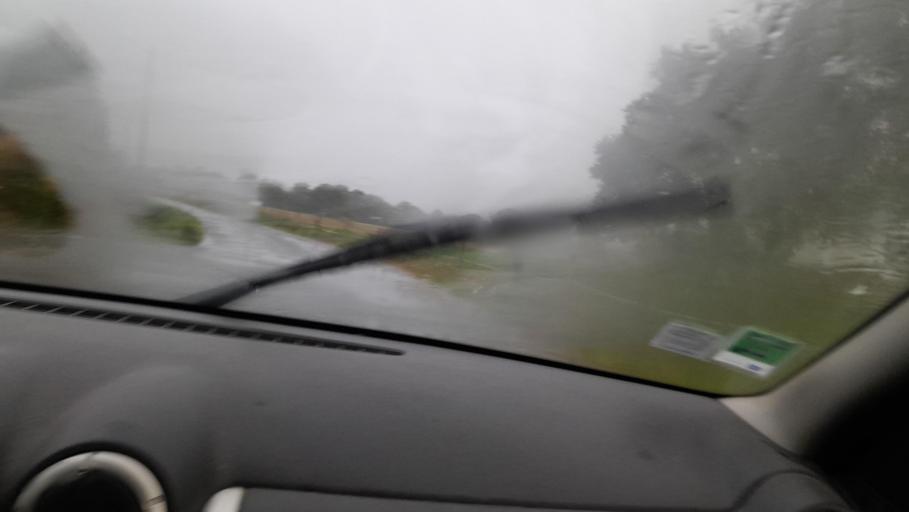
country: FR
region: Pays de la Loire
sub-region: Departement de la Mayenne
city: Ballots
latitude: 47.8566
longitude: -1.0596
